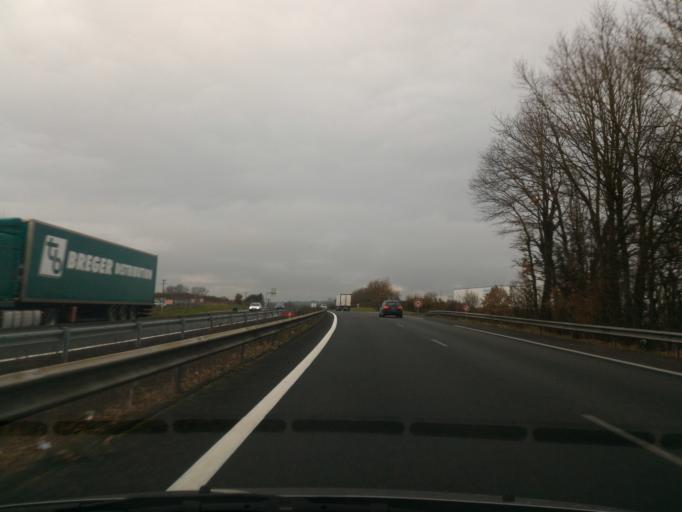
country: FR
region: Poitou-Charentes
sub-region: Departement de la Vienne
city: Iteuil
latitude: 46.4992
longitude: 0.2784
